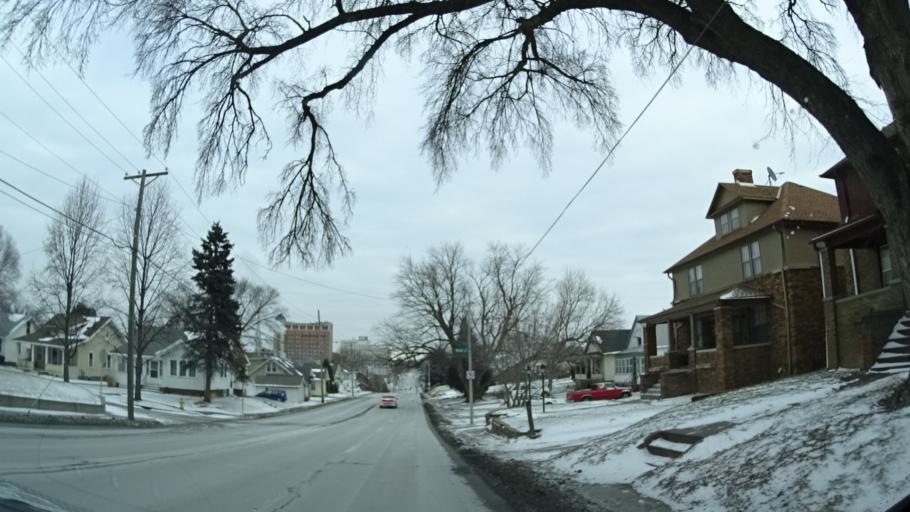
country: US
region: Nebraska
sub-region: Douglas County
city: Omaha
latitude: 41.2491
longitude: -95.9757
